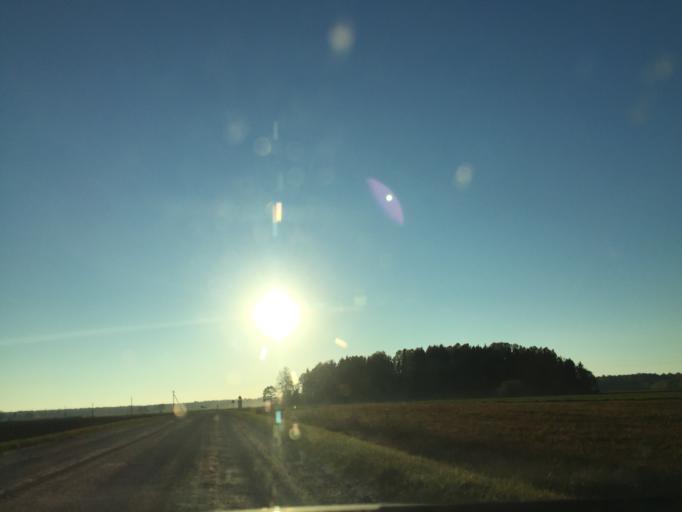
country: LT
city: Vieksniai
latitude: 56.3095
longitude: 22.5457
